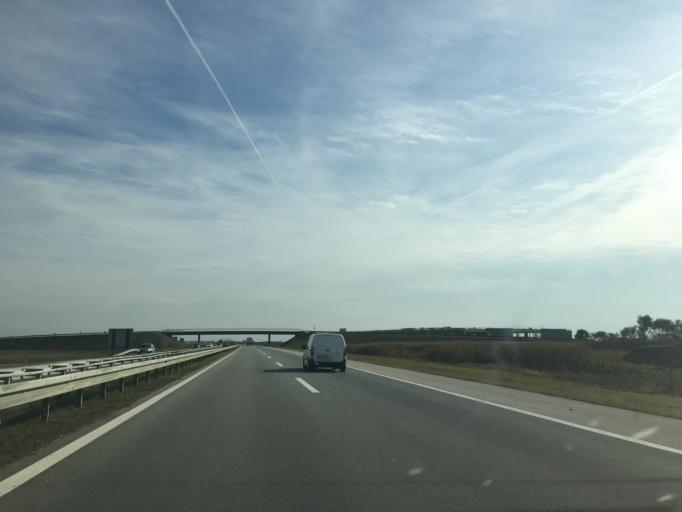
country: RS
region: Autonomna Pokrajina Vojvodina
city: Nova Pazova
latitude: 44.9694
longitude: 20.2355
